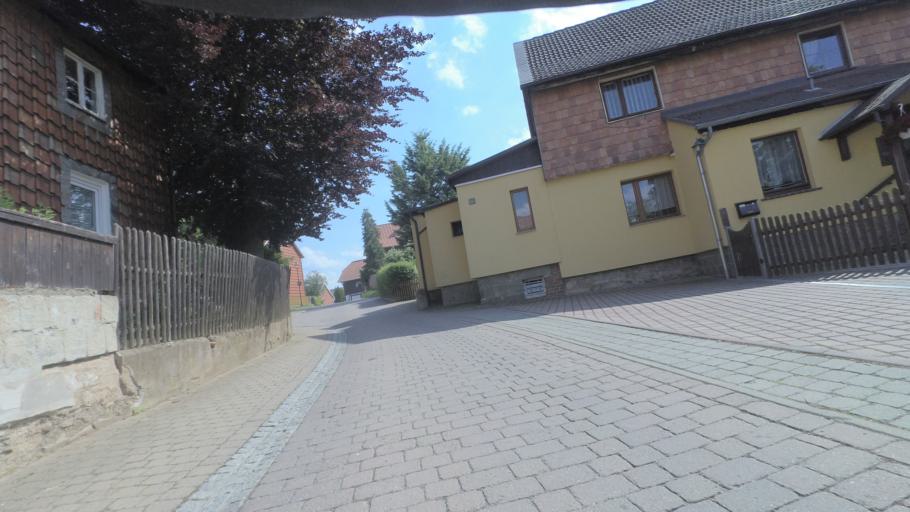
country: DE
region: Saxony-Anhalt
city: Darlingerode
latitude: 51.8456
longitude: 10.7292
